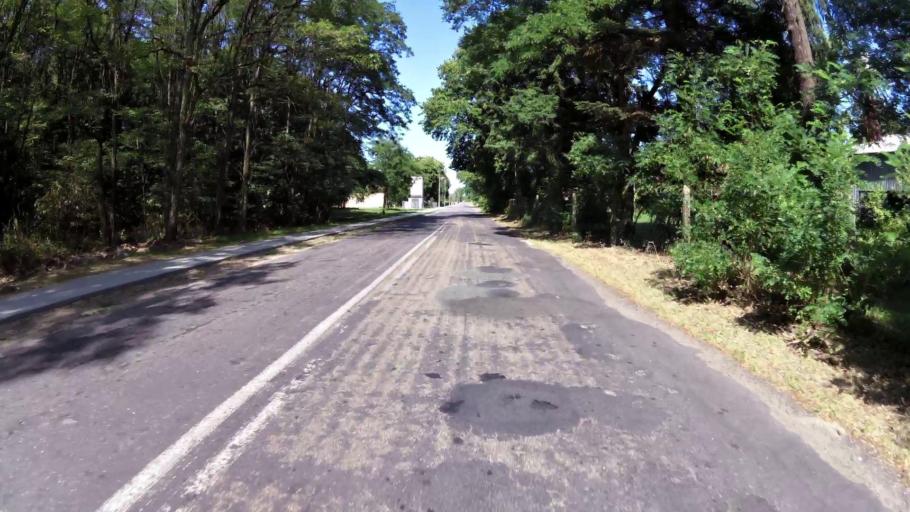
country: PL
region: West Pomeranian Voivodeship
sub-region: Powiat stargardzki
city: Dobrzany
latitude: 53.3373
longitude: 15.3940
